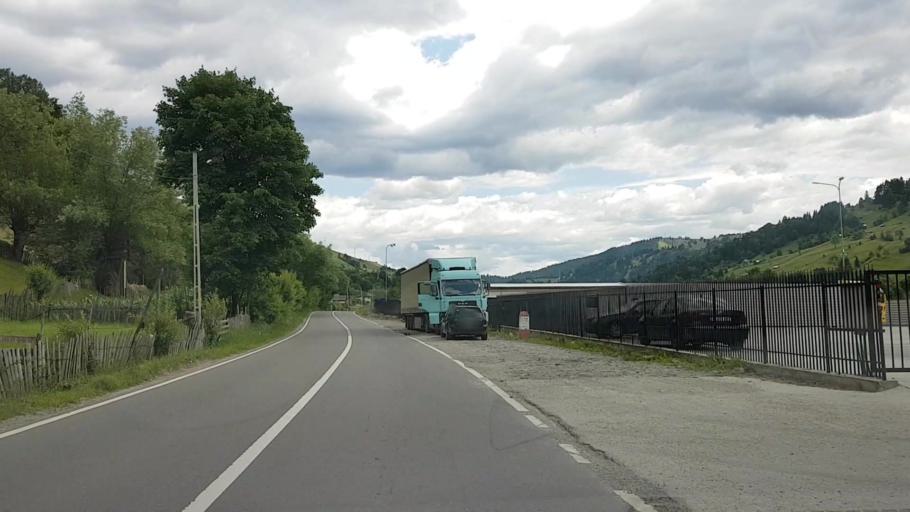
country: RO
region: Neamt
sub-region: Comuna Borca
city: Borca
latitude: 47.1706
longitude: 25.7971
